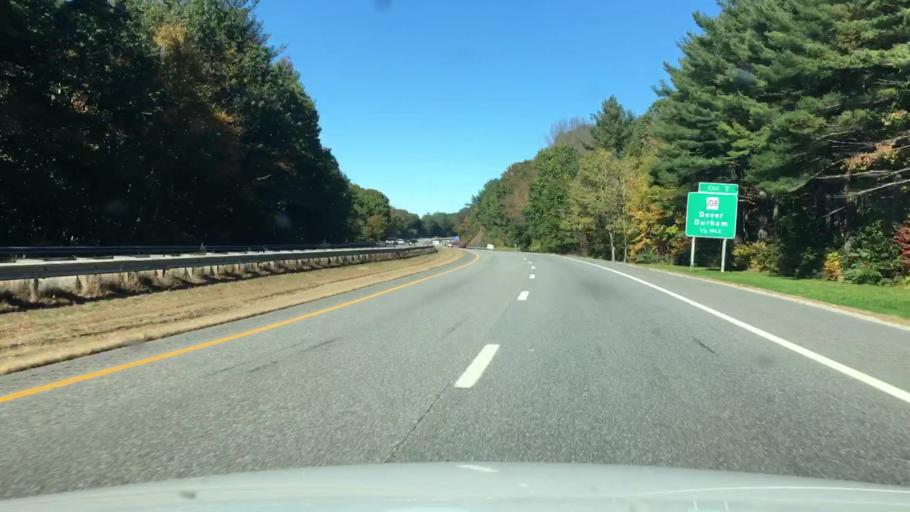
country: US
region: New Hampshire
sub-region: Strafford County
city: Dover
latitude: 43.1725
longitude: -70.8634
